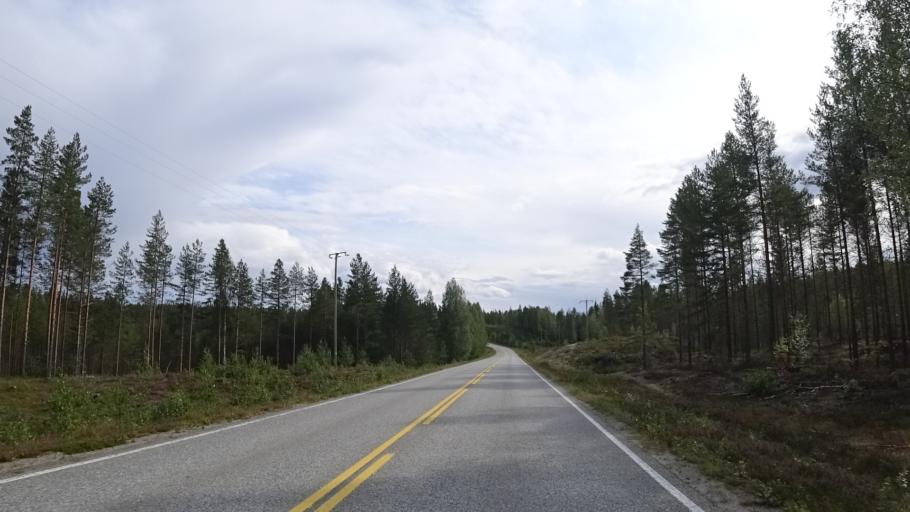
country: FI
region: North Karelia
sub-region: Joensuu
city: Ilomantsi
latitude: 62.6322
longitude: 31.0935
